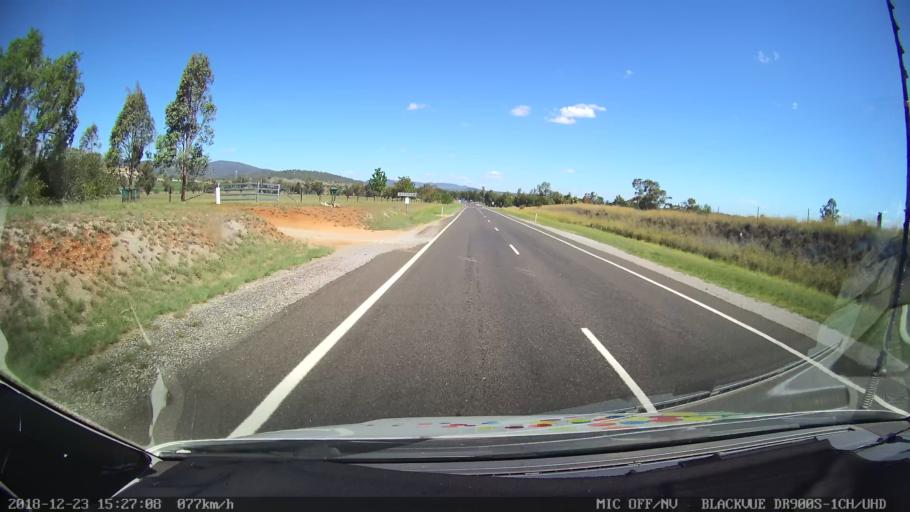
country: AU
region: New South Wales
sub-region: Tamworth Municipality
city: East Tamworth
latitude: -30.9246
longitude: 150.8434
